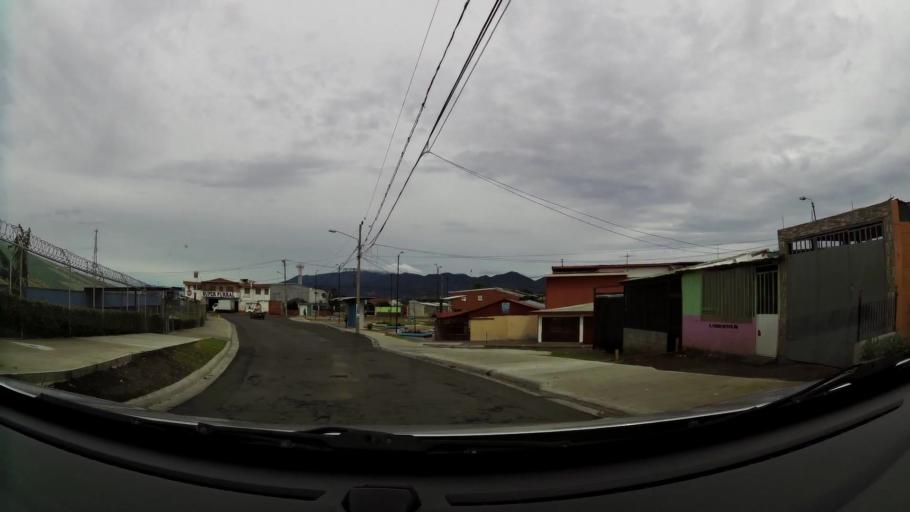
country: CR
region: San Jose
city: Ipis
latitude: 9.9610
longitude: -84.0110
